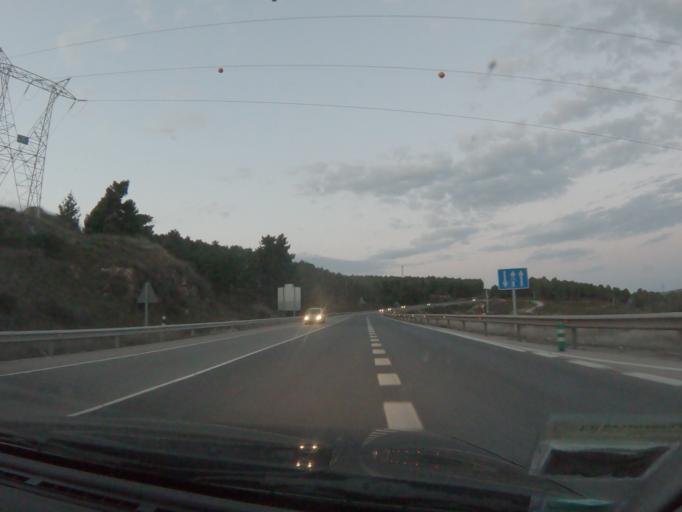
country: ES
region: Castille and Leon
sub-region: Provincia de Leon
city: Ponferrada
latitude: 42.5554
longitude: -6.5615
